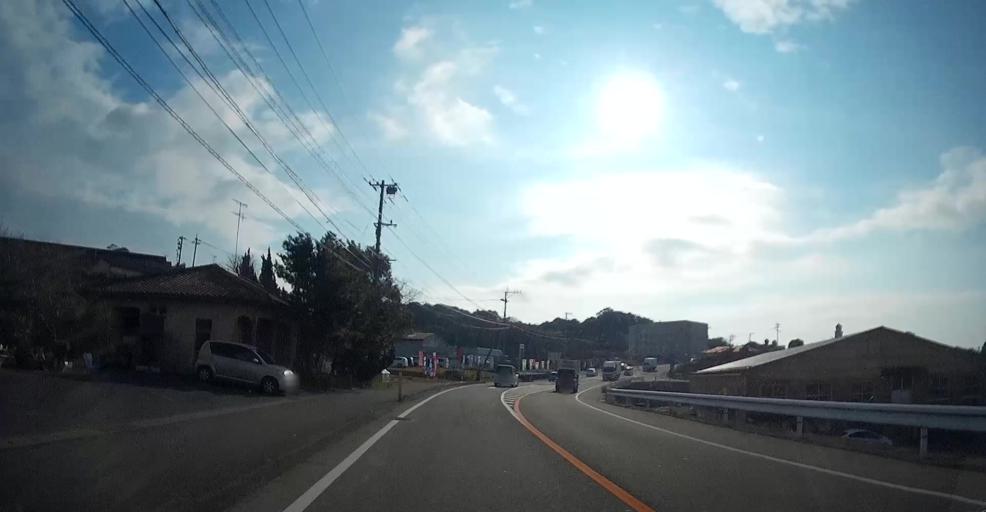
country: JP
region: Kumamoto
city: Yatsushiro
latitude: 32.5730
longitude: 130.4195
